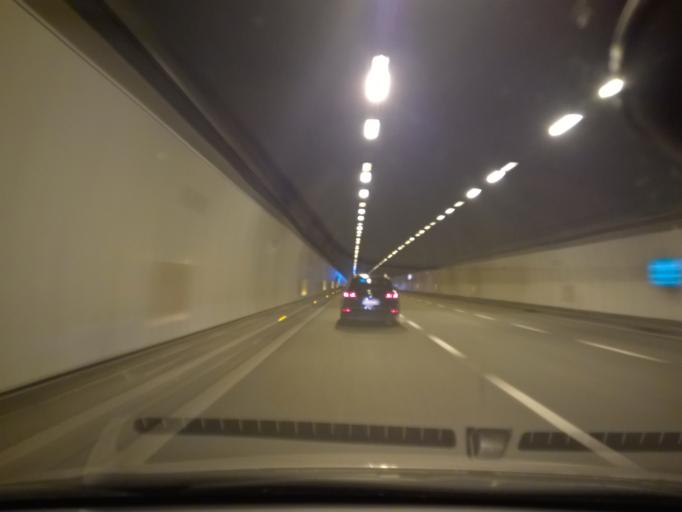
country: IT
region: Veneto
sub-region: Provincia di Vicenza
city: Arcugnano-Torri
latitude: 45.5162
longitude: 11.5445
